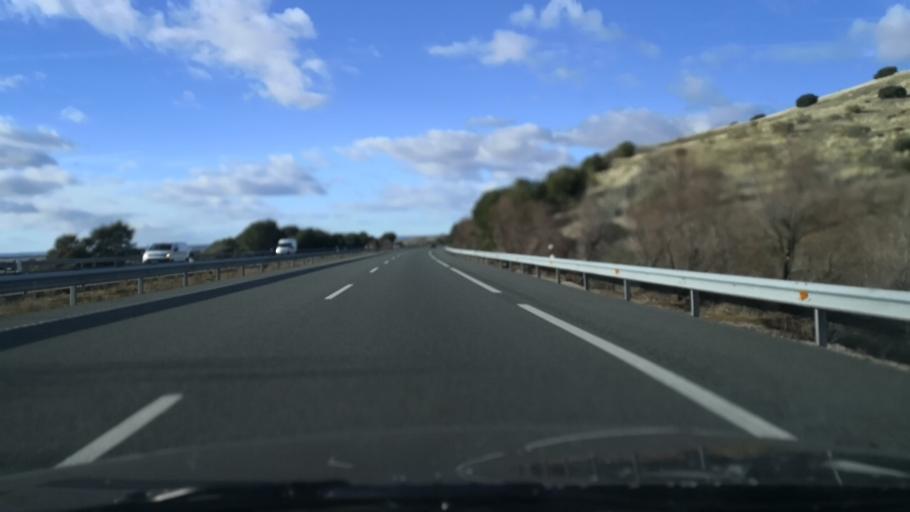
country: ES
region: Castille and Leon
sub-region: Provincia de Segovia
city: Labajos
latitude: 40.8392
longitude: -4.5345
